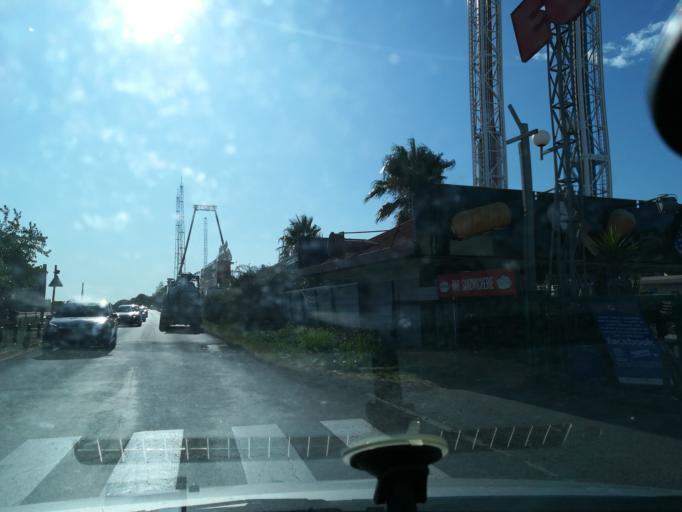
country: FR
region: Languedoc-Roussillon
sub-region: Departement de l'Herault
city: Vias
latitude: 43.3010
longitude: 3.4131
